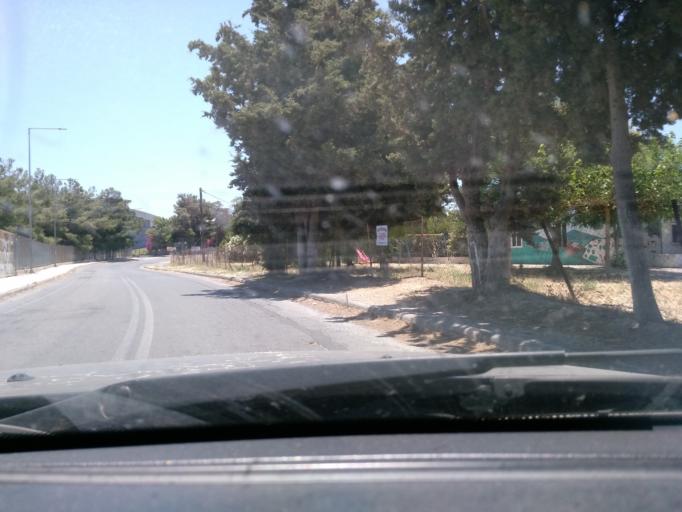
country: GR
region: Crete
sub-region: Nomos Irakleiou
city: Gazi
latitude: 35.3171
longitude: 25.1012
